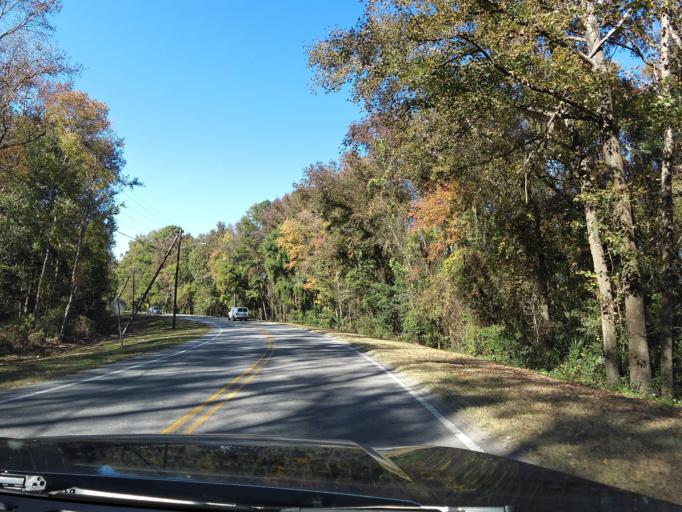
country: US
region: Georgia
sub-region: Chatham County
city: Savannah
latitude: 32.0761
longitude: -81.1259
